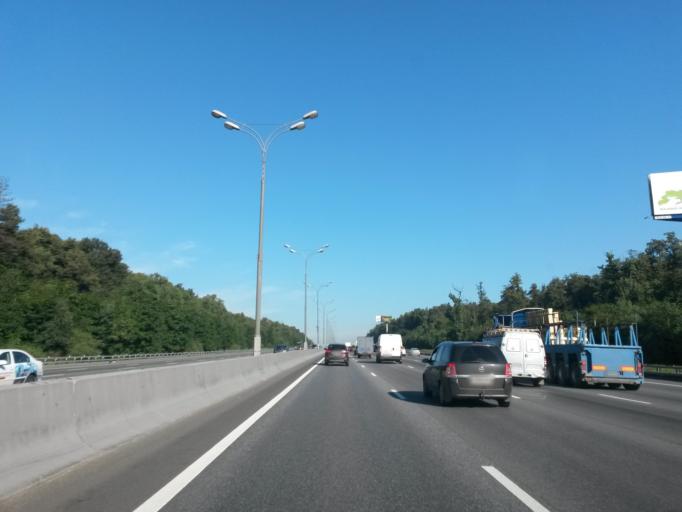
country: RU
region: Moscow
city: Gol'yanovo
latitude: 55.8342
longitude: 37.8199
